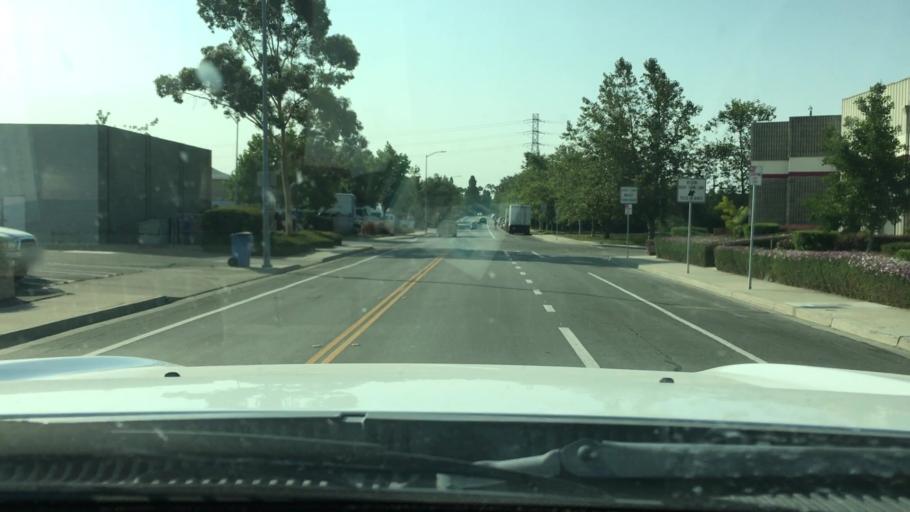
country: US
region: California
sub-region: San Luis Obispo County
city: San Luis Obispo
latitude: 35.2575
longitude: -120.6450
